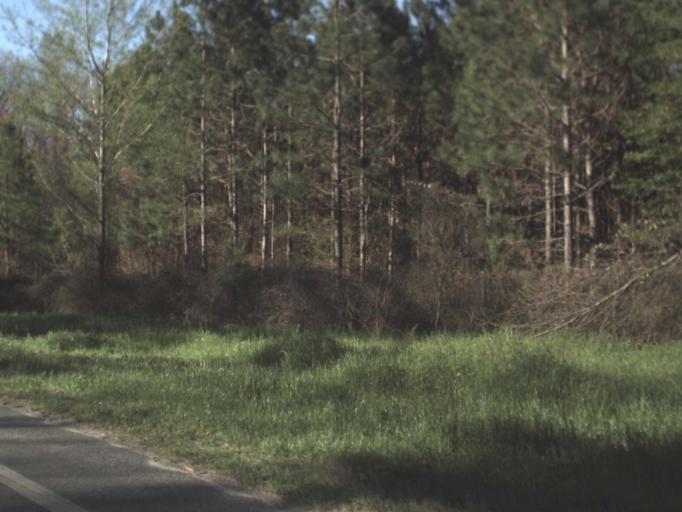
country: US
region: Georgia
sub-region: Brooks County
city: Quitman
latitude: 30.6508
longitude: -83.6426
